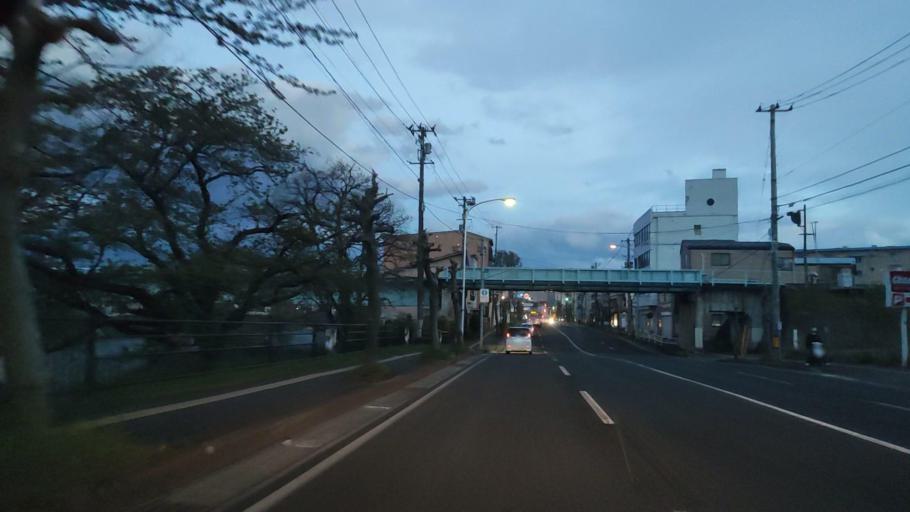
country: JP
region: Iwate
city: Morioka-shi
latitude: 39.7113
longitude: 141.1319
